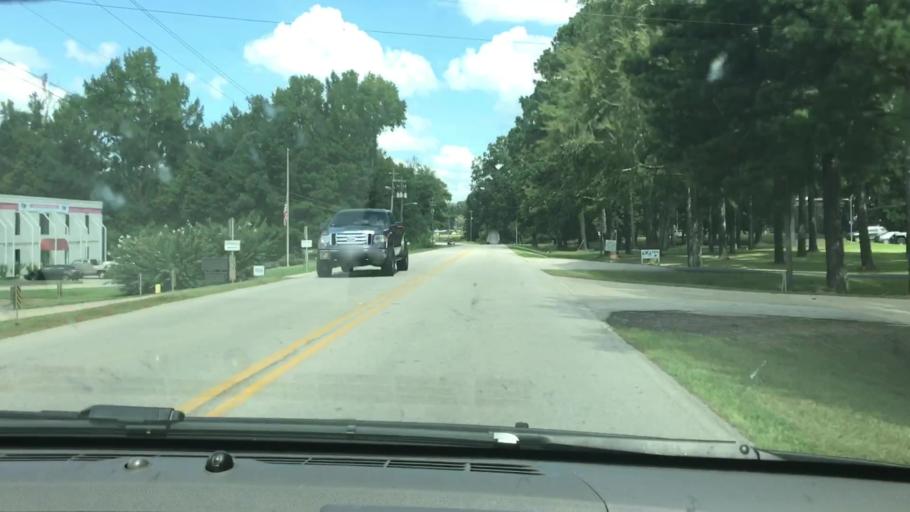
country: US
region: Georgia
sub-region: Troup County
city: La Grange
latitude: 33.0149
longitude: -85.0664
